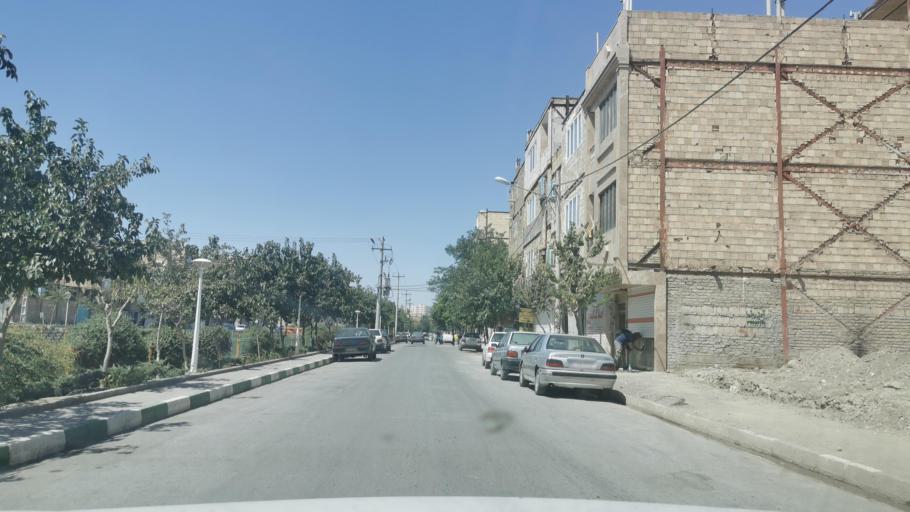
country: IR
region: Razavi Khorasan
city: Mashhad
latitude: 36.3589
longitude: 59.5623
